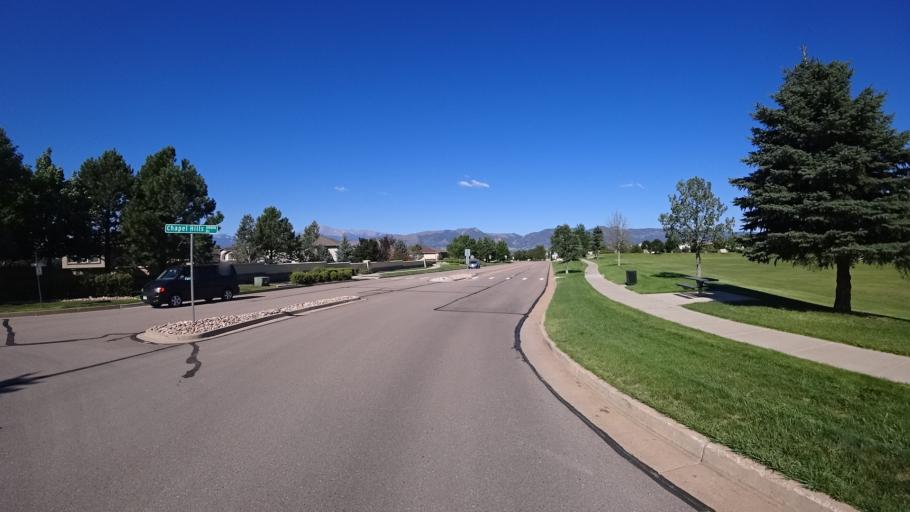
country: US
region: Colorado
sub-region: El Paso County
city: Black Forest
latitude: 38.9758
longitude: -104.7757
